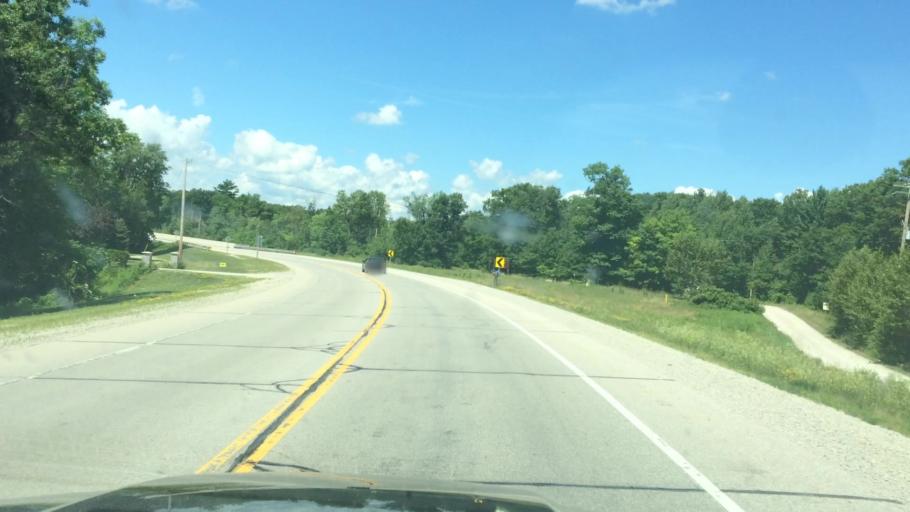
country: US
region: Wisconsin
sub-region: Marinette County
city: Peshtigo
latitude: 45.1060
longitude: -87.7518
